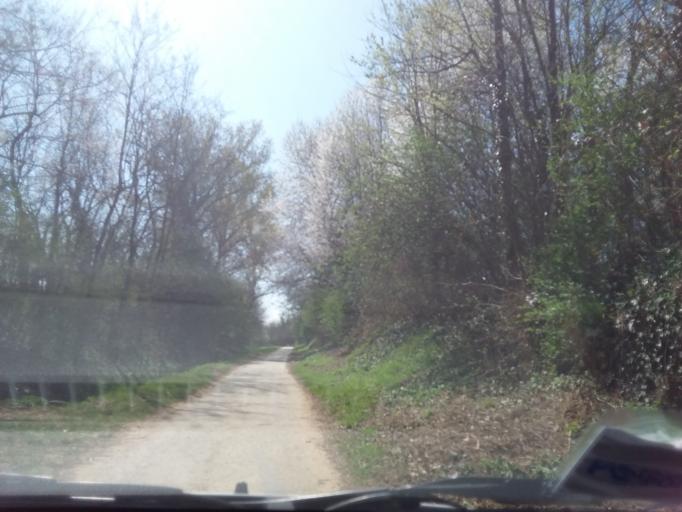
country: IT
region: Piedmont
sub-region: Provincia di Torino
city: Rivoli
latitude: 45.0567
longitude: 7.5155
